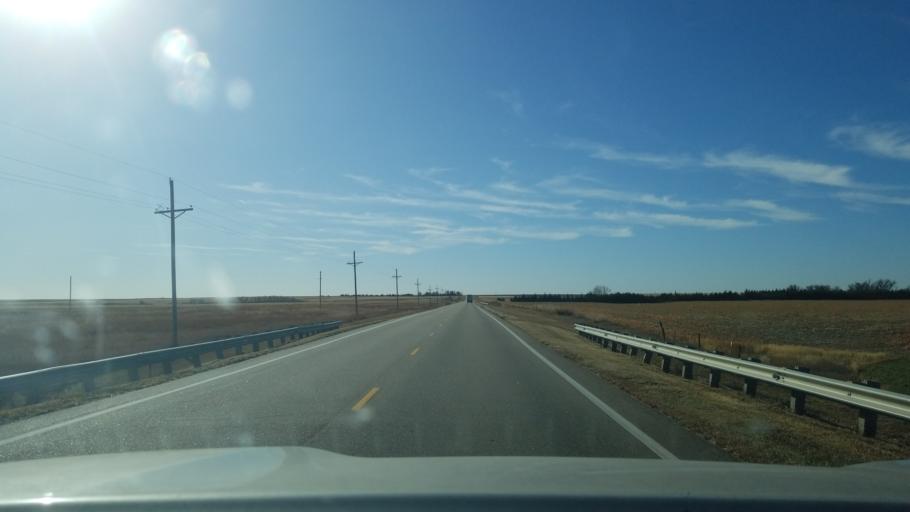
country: US
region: Kansas
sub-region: Ness County
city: Ness City
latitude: 38.4149
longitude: -99.8985
